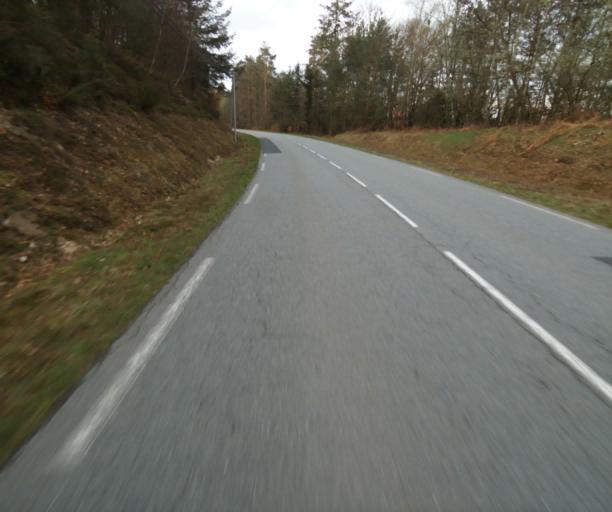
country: FR
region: Limousin
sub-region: Departement de la Correze
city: Correze
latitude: 45.3921
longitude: 1.8627
